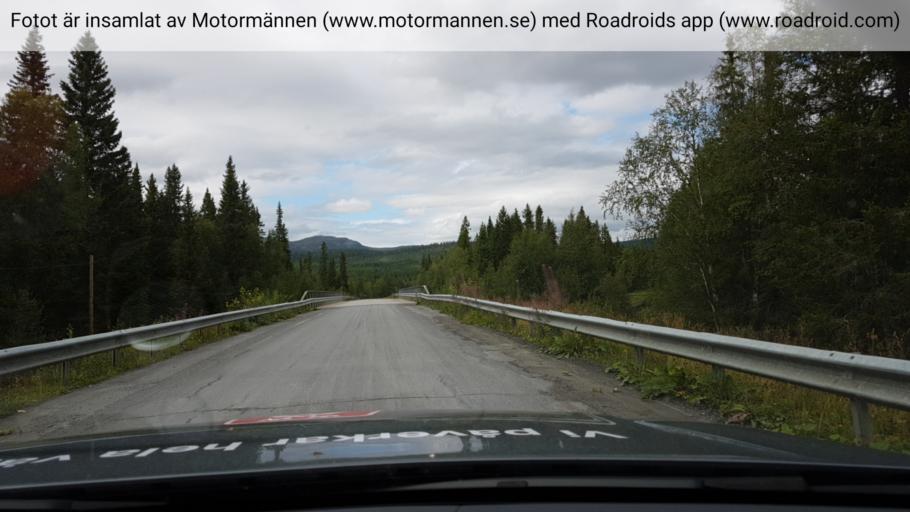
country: SE
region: Jaemtland
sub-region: Krokoms Kommun
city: Valla
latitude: 63.7020
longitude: 13.5980
